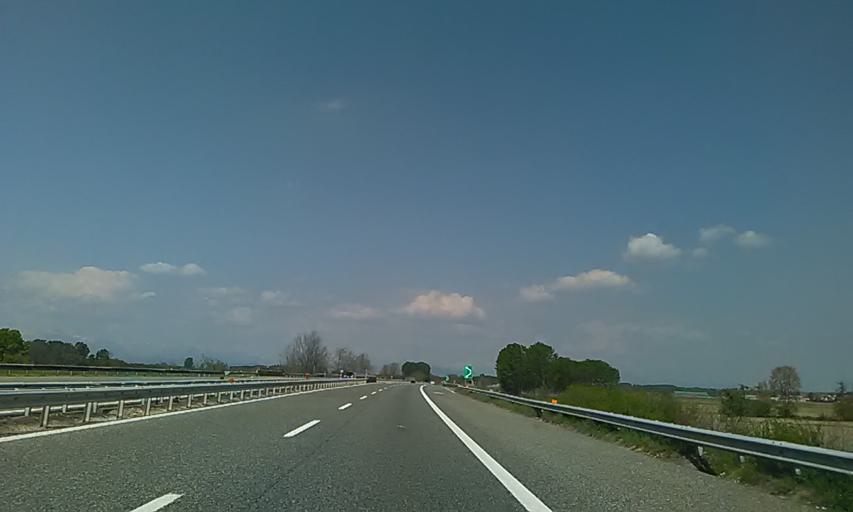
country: IT
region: Piedmont
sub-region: Provincia di Novara
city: Sillavengo
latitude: 45.5085
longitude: 8.4337
